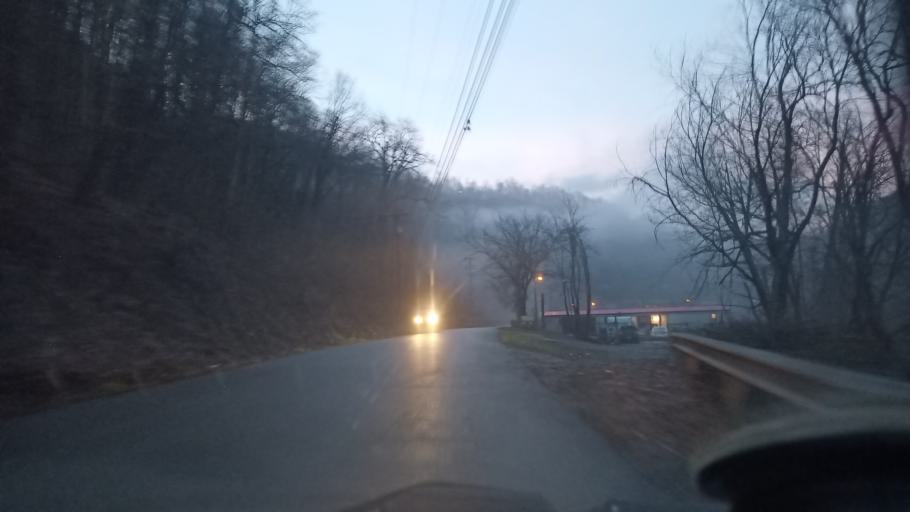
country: US
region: West Virginia
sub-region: Logan County
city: Mallory
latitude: 37.7268
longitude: -81.8772
